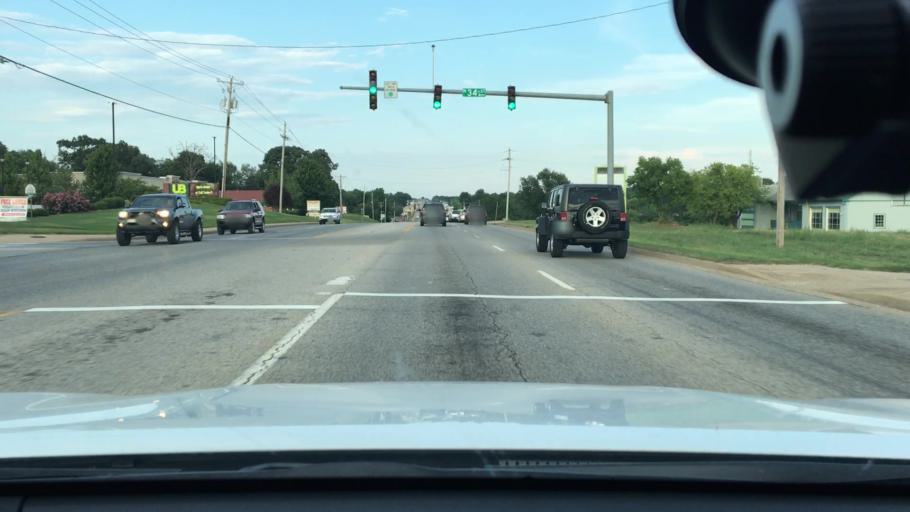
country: US
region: Arkansas
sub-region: Benton County
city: Rogers
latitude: 36.3345
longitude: -94.1668
